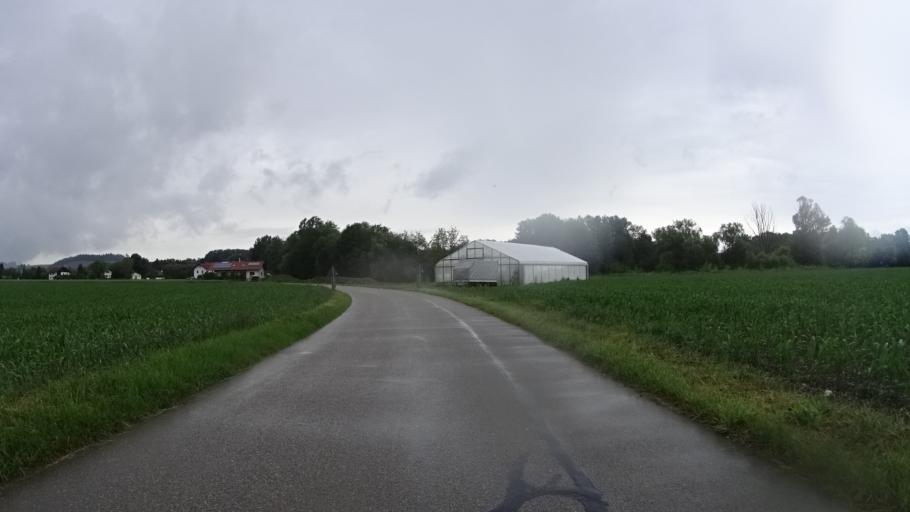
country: DE
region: Bavaria
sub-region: Lower Bavaria
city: Pocking
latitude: 48.4089
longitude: 13.2876
